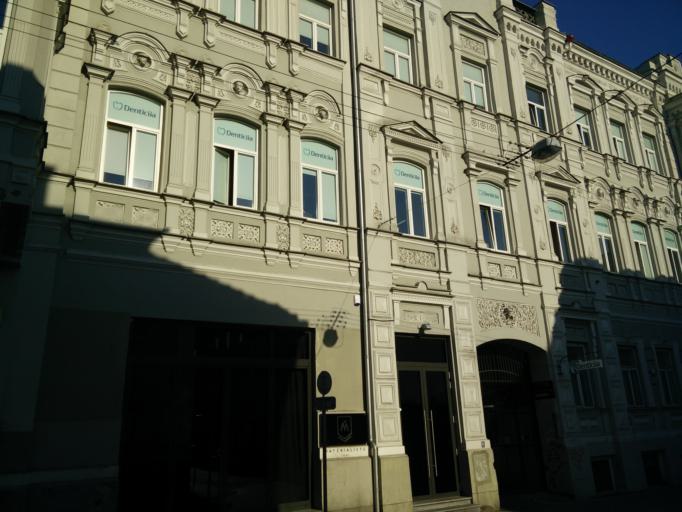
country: LT
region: Vilnius County
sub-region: Vilnius
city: Vilnius
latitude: 54.6850
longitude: 25.2795
